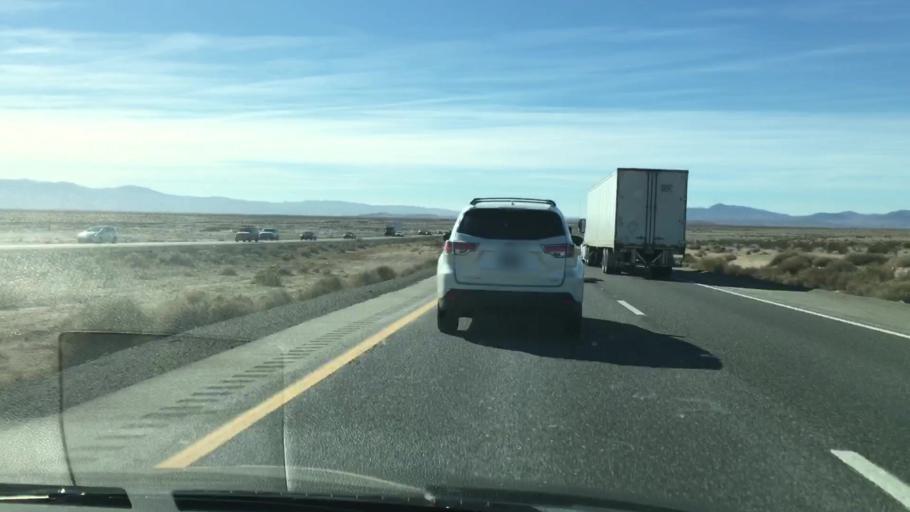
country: US
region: California
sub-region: San Bernardino County
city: Fort Irwin
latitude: 35.0003
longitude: -116.5613
